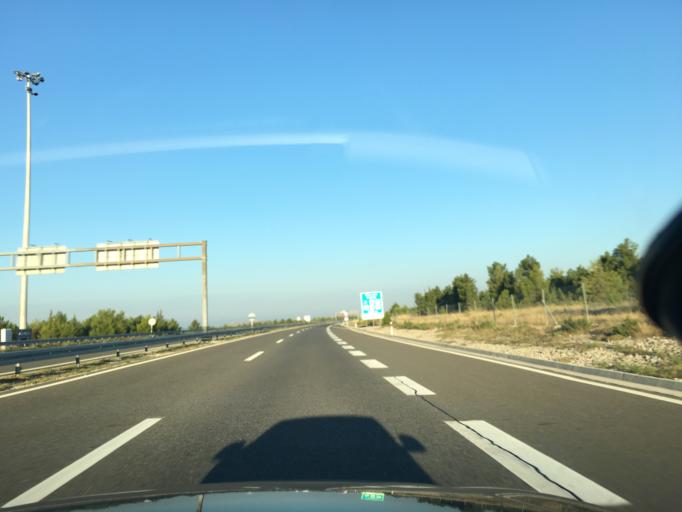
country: HR
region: Sibensko-Kniniska
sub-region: Grad Sibenik
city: Brodarica
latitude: 43.6839
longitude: 16.0572
